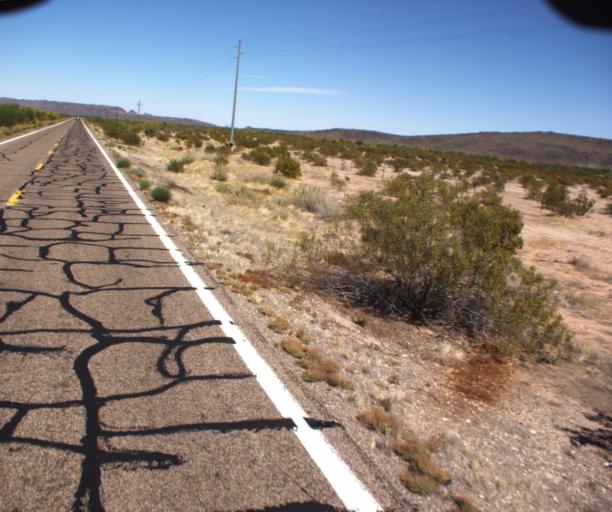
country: US
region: Arizona
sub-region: Pima County
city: Ajo
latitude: 32.4786
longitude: -112.8783
